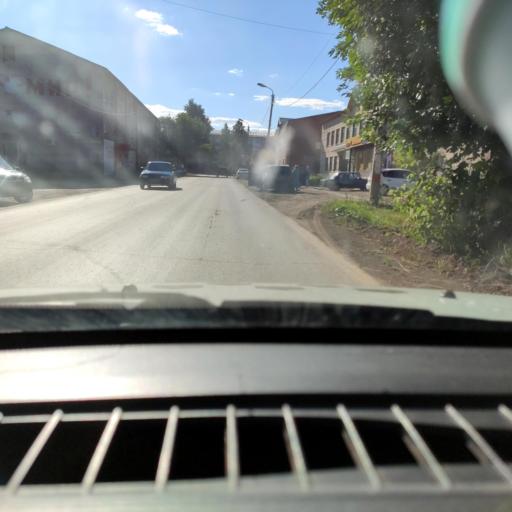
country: RU
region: Perm
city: Ocher
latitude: 57.8829
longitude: 54.7147
